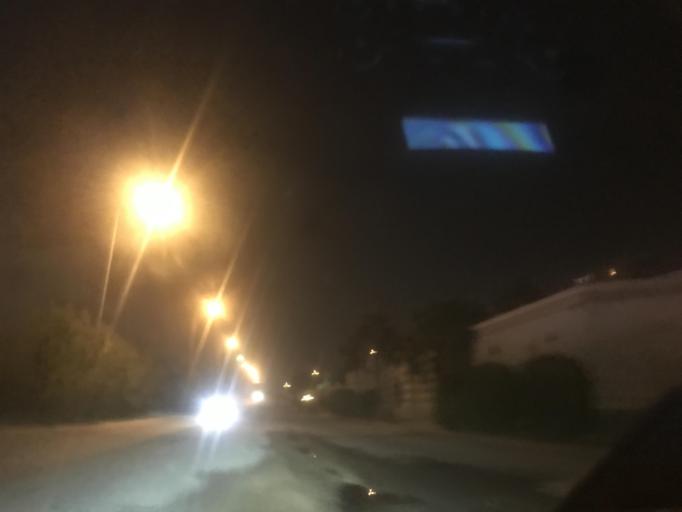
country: SA
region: Ar Riyad
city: Riyadh
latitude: 24.7703
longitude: 46.5942
